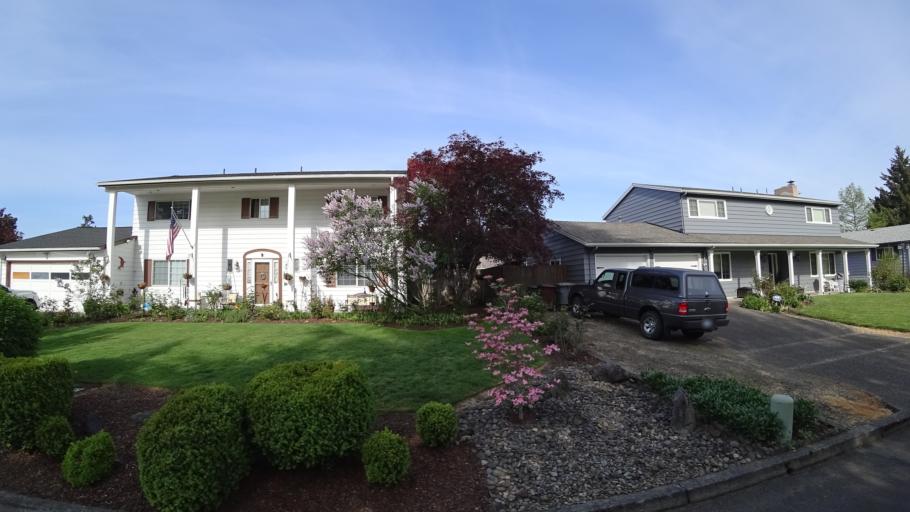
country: US
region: Oregon
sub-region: Washington County
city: Hillsboro
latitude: 45.5248
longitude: -122.9648
